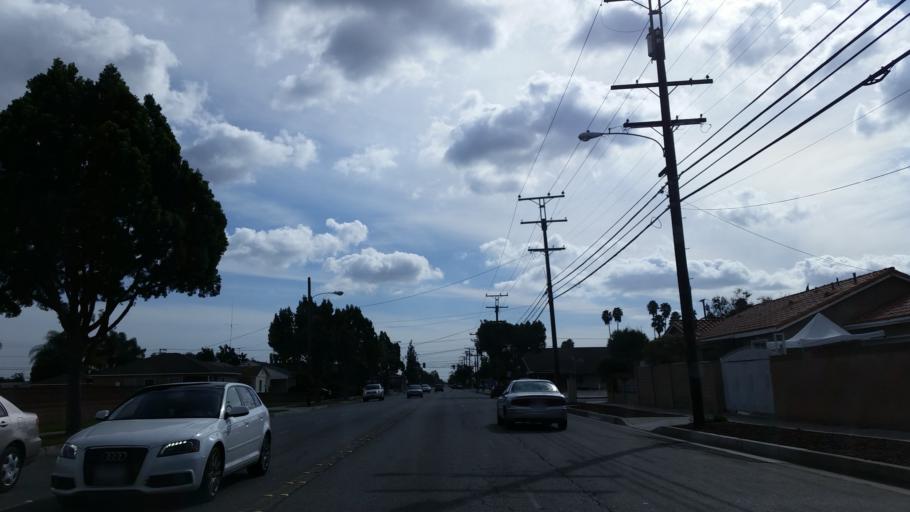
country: US
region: California
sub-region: Los Angeles County
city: Bellflower
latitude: 33.8987
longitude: -118.1341
